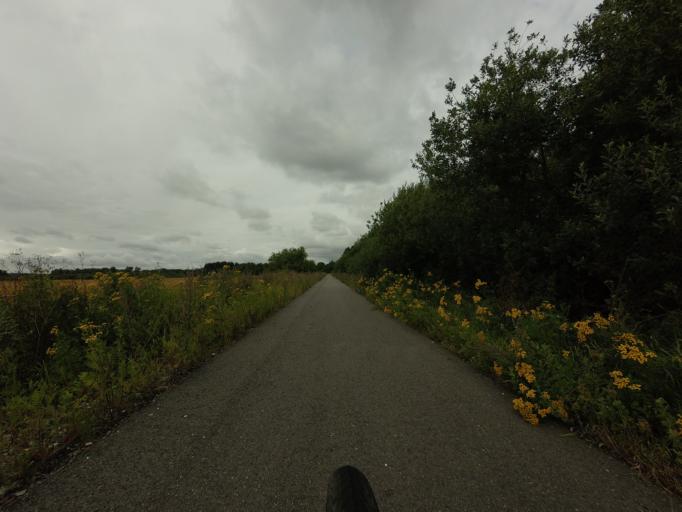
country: DK
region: Central Jutland
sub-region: Syddjurs Kommune
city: Ryomgard
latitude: 56.3849
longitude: 10.4610
